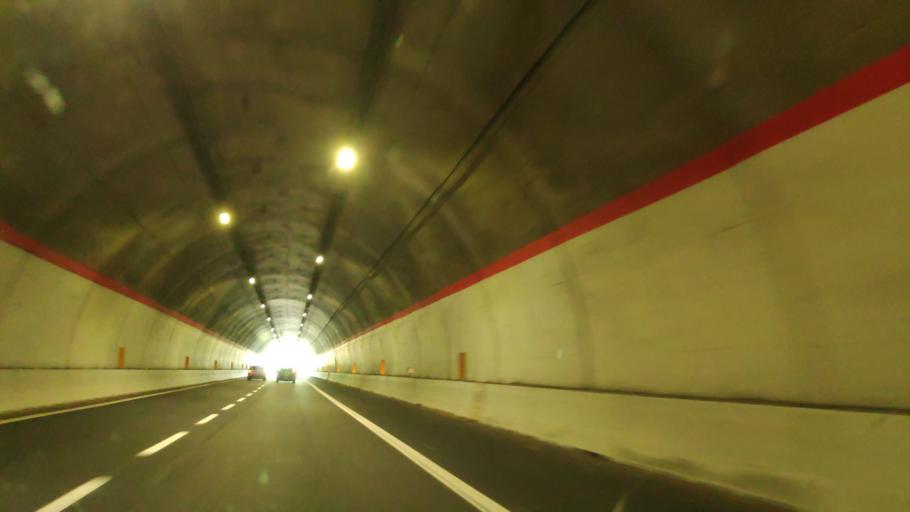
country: IT
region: Campania
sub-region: Provincia di Salerno
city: Auletta
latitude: 40.5353
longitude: 15.4222
